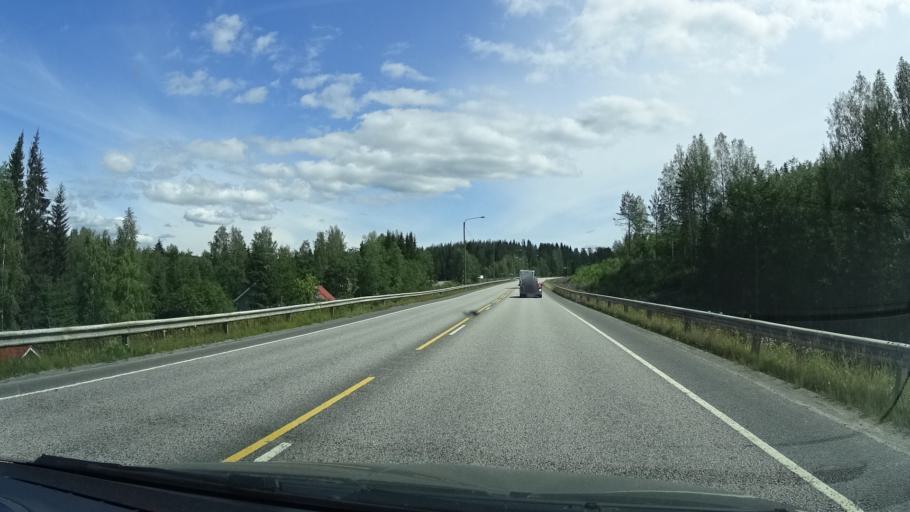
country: FI
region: Central Finland
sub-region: Jyvaeskylae
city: Jyvaeskylae
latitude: 62.2649
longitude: 25.5735
